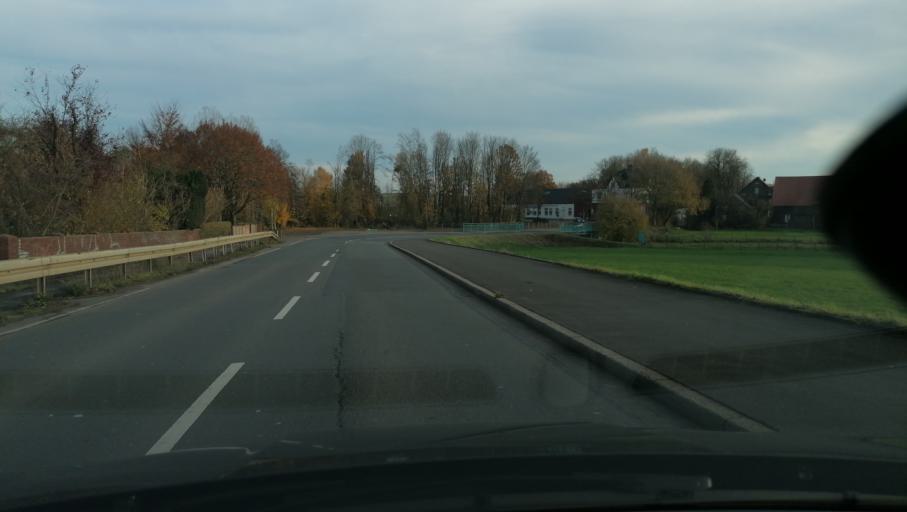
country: DE
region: North Rhine-Westphalia
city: Waltrop
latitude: 51.5499
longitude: 7.3979
